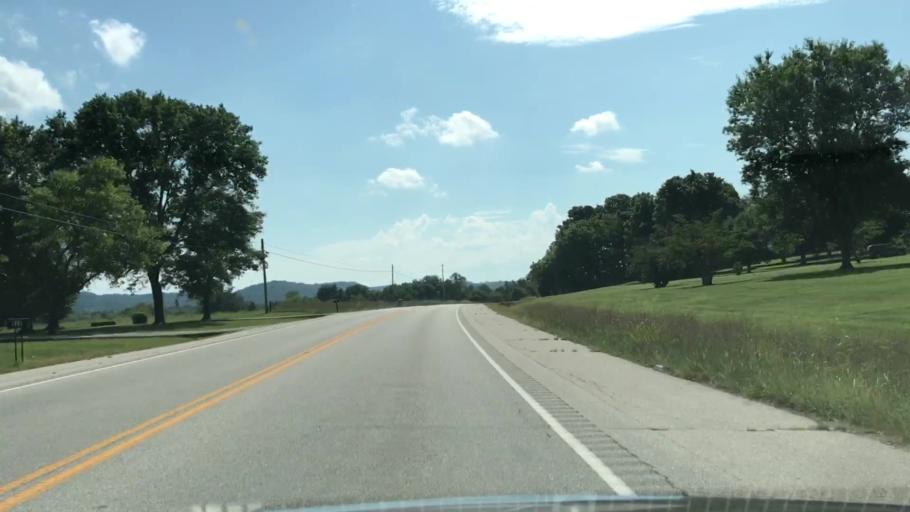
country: US
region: Tennessee
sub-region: Trousdale County
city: Hartsville
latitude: 36.3579
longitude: -86.0470
